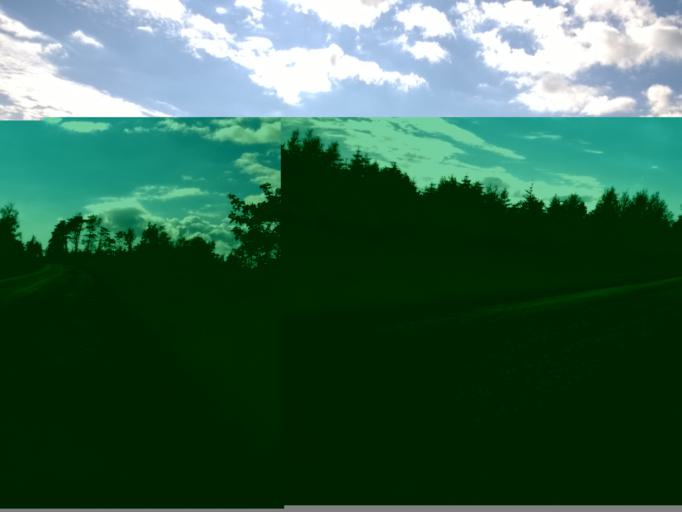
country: DK
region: Central Jutland
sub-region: Holstebro Kommune
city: Vinderup
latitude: 56.5108
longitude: 8.8217
